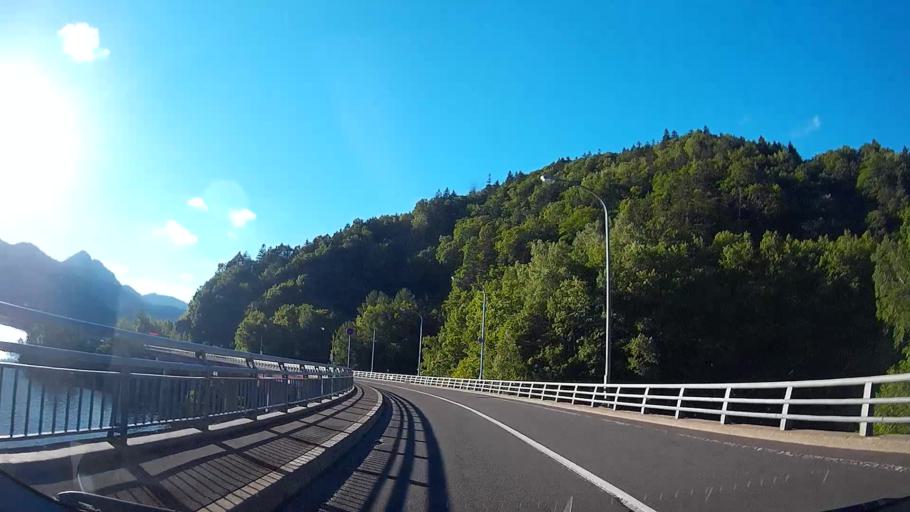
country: JP
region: Hokkaido
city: Sapporo
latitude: 42.9900
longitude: 141.1635
